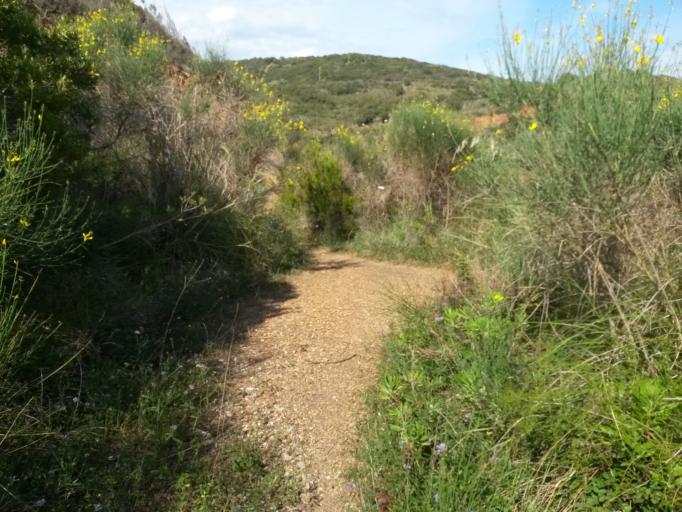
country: IT
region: Tuscany
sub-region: Provincia di Livorno
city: Porto Azzurro
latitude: 42.7734
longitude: 10.4186
